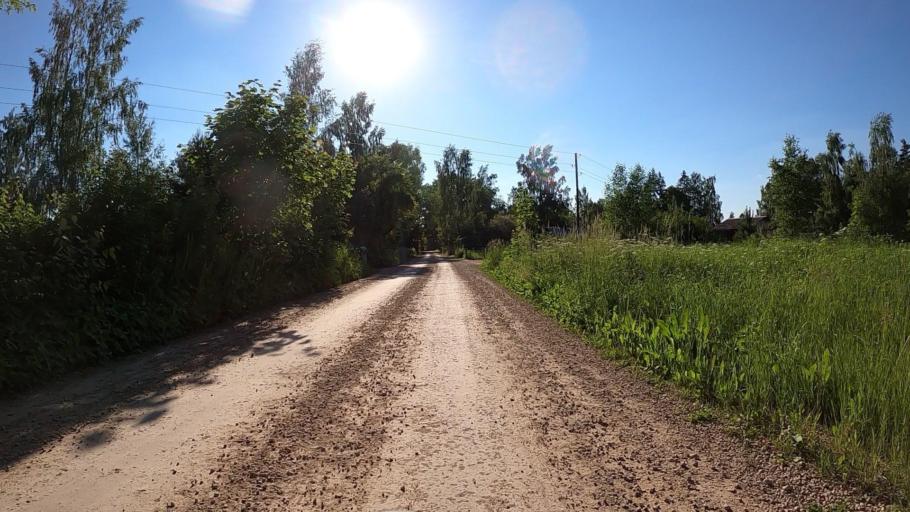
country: LV
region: Kekava
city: Kekava
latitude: 56.8732
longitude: 24.2759
